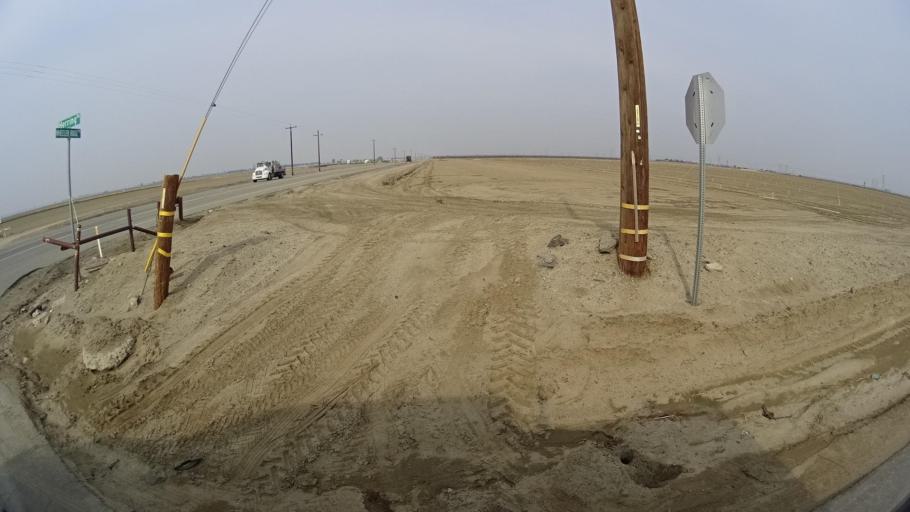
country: US
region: California
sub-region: Kern County
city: Weedpatch
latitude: 35.1511
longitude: -118.9144
